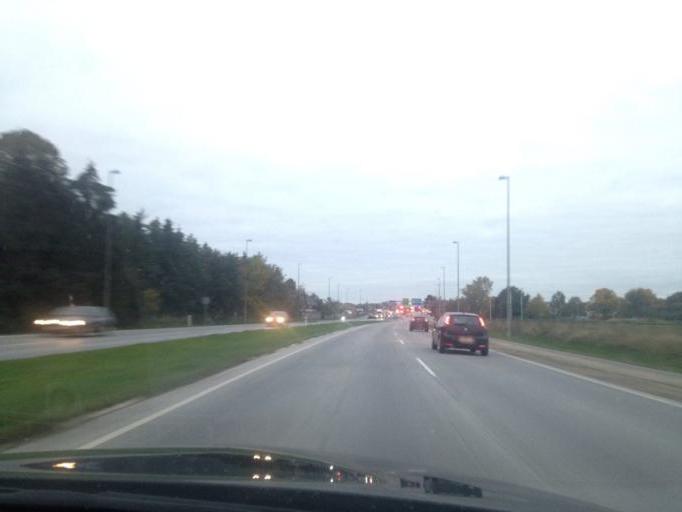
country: DK
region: Zealand
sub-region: Roskilde Kommune
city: Roskilde
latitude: 55.6207
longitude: 12.0929
